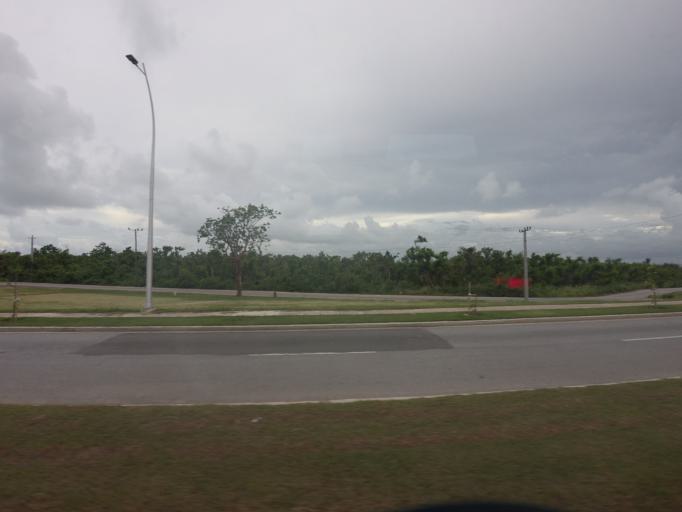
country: CU
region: Matanzas
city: Varadero
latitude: 23.1956
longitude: -81.1434
